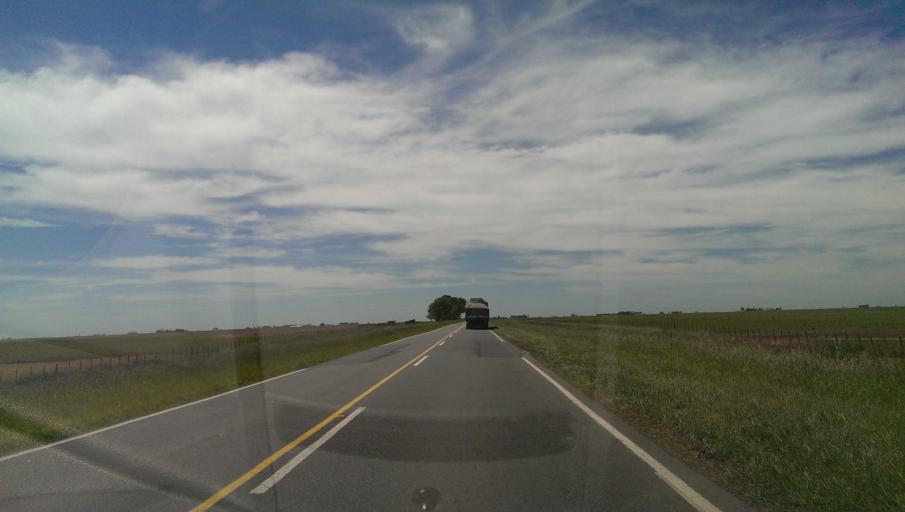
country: AR
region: Buenos Aires
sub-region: Partido de General La Madrid
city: General La Madrid
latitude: -37.4243
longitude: -61.0656
